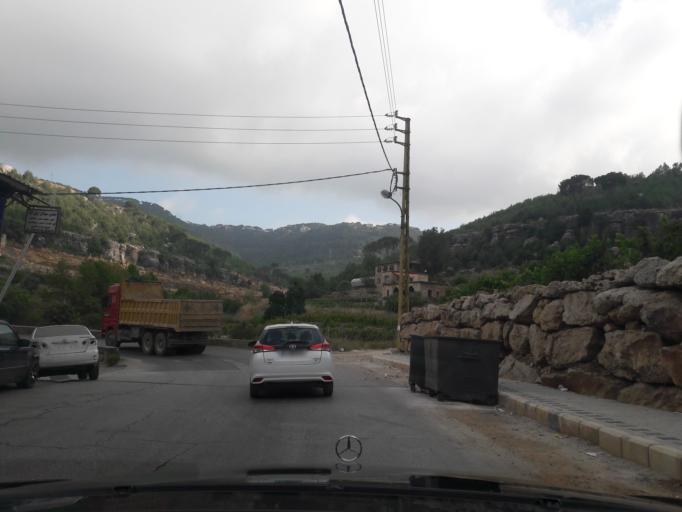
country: LB
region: Mont-Liban
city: Djounie
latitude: 33.9225
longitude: 35.7295
